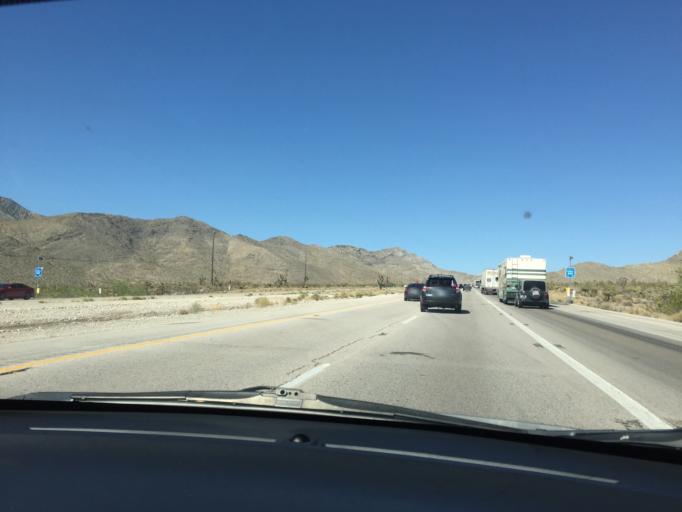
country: US
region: Nevada
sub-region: Clark County
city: Sandy Valley
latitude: 35.4680
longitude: -115.6055
